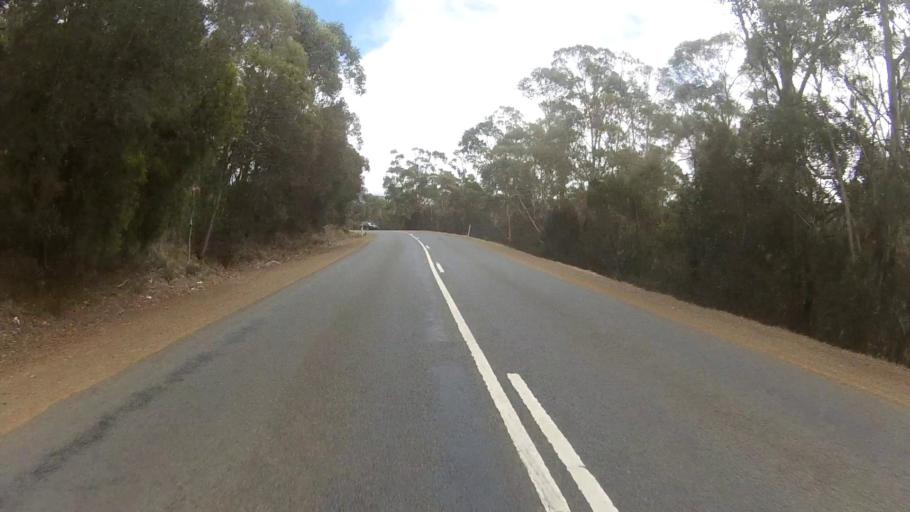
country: AU
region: Tasmania
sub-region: Kingborough
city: Margate
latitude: -43.0072
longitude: 147.2425
